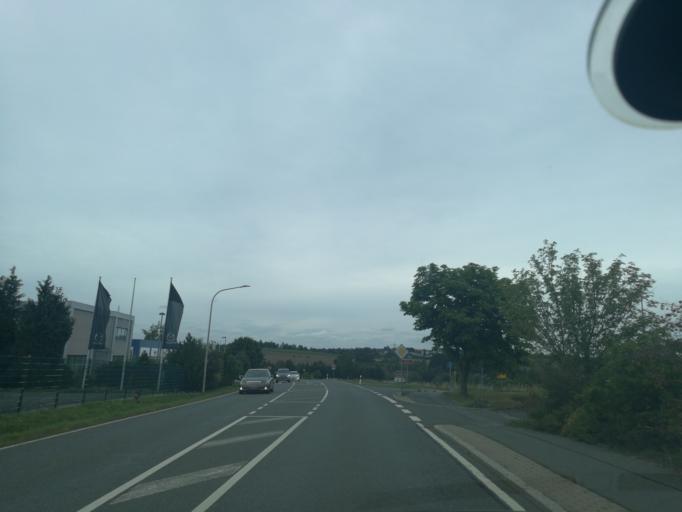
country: DE
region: Bavaria
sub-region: Upper Franconia
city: Dohlau
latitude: 50.2899
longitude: 11.9443
